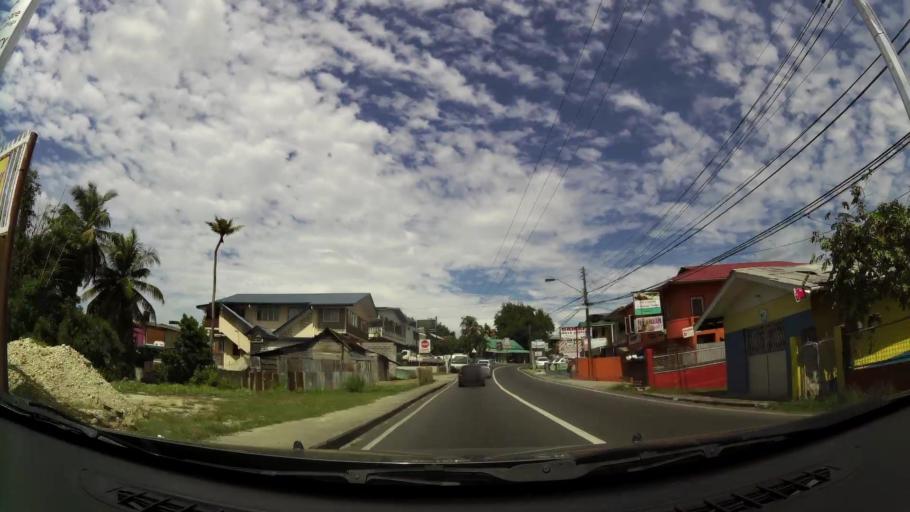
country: TT
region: City of San Fernando
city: Marabella
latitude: 10.2964
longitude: -61.4543
